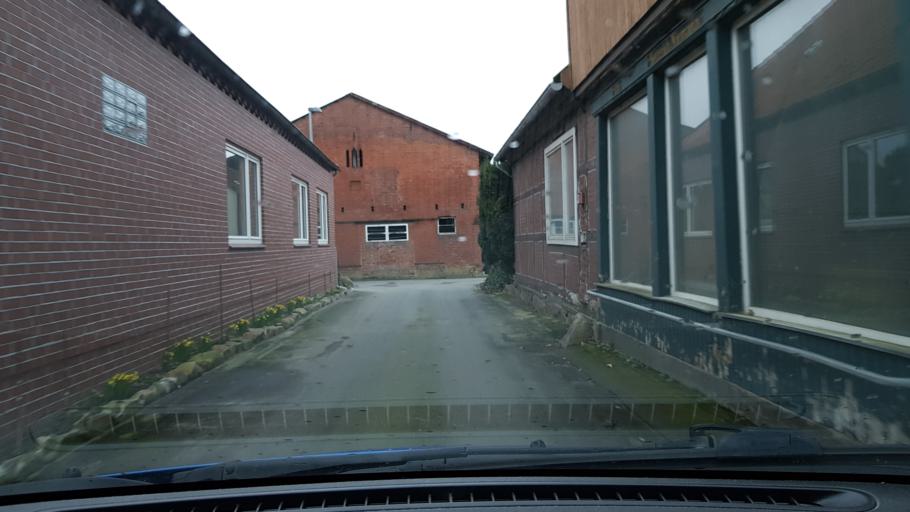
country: DE
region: Lower Saxony
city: Emmendorf
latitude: 53.0045
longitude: 10.6046
